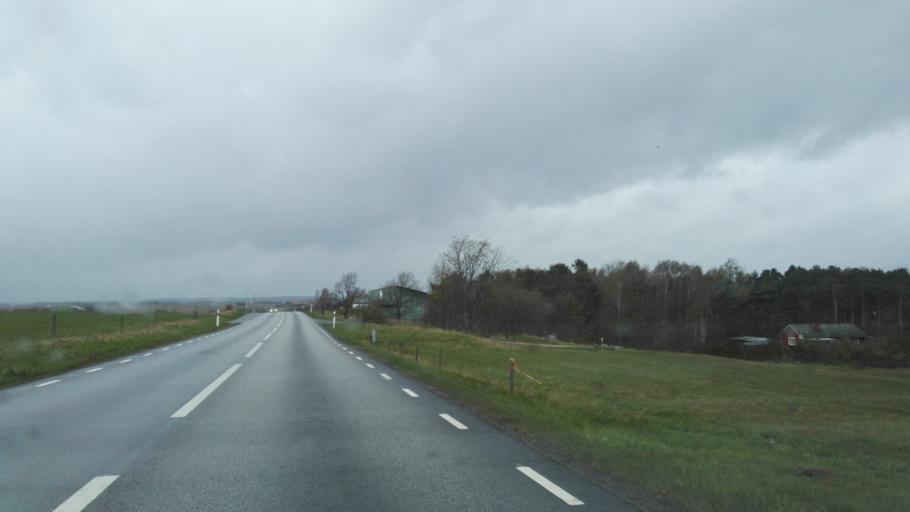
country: SE
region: Skane
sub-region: Simrishamns Kommun
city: Kivik
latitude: 55.6946
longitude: 14.2052
